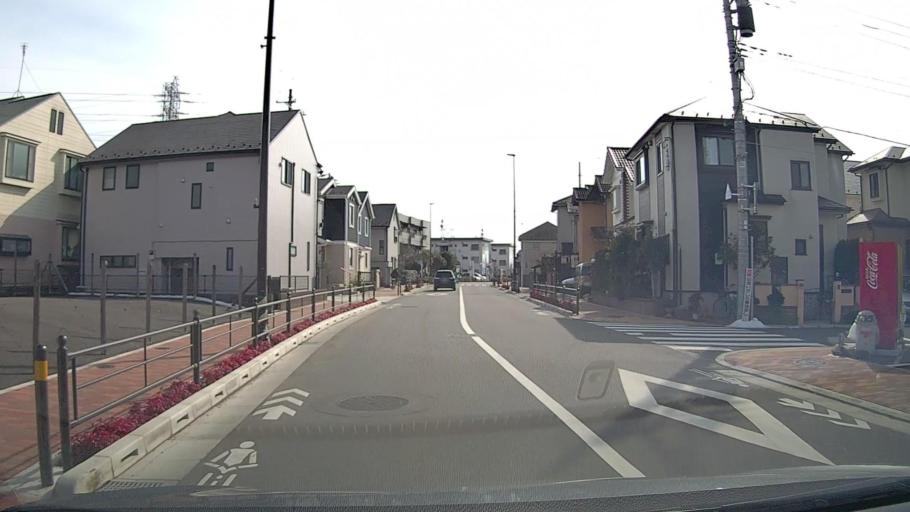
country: JP
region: Tokyo
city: Tanashicho
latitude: 35.7591
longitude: 139.5667
